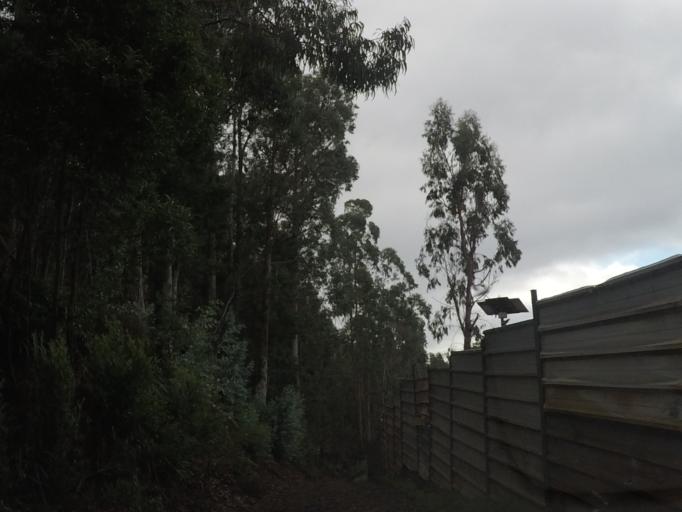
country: PT
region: Madeira
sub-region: Funchal
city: Nossa Senhora do Monte
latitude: 32.6780
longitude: -16.8776
